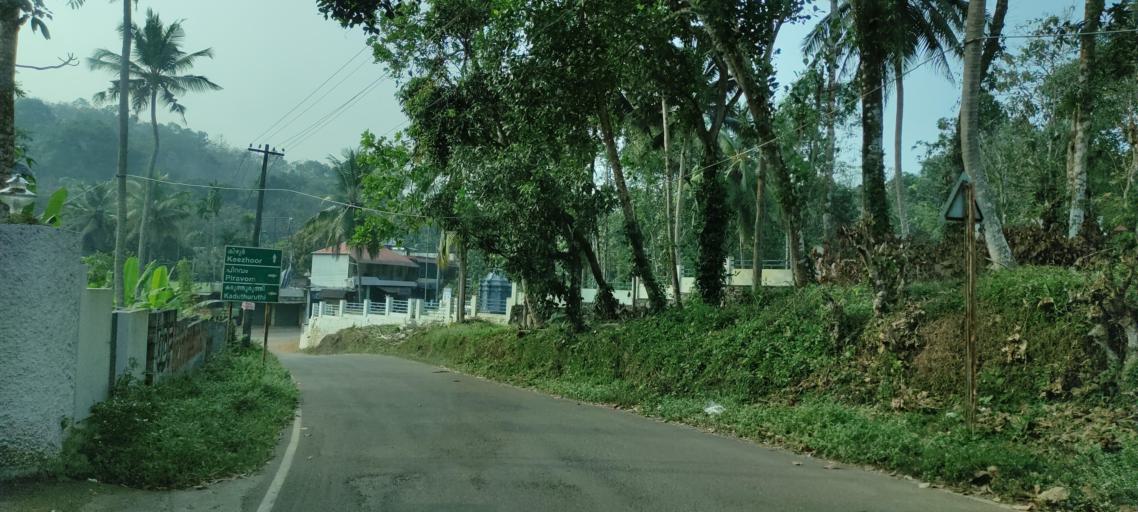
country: IN
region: Kerala
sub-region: Ernakulam
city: Piravam
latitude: 9.8010
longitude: 76.4991
